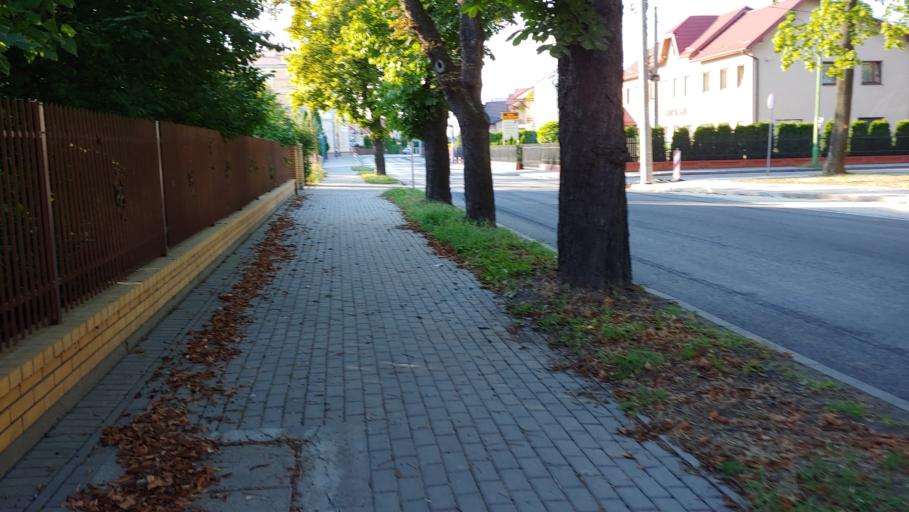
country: PL
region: Subcarpathian Voivodeship
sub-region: Powiat mielecki
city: Mielec
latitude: 50.2893
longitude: 21.4153
